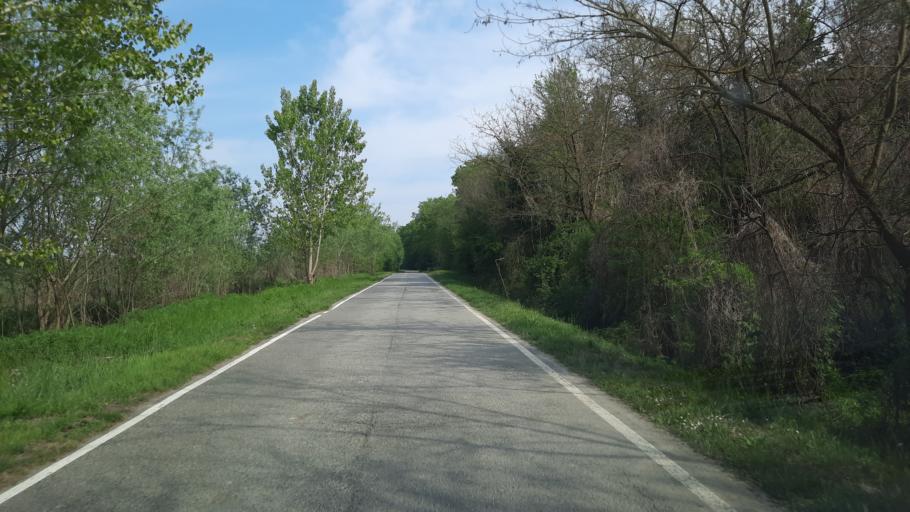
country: IT
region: Piedmont
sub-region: Provincia di Alessandria
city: Camino
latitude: 45.1766
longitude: 8.2743
